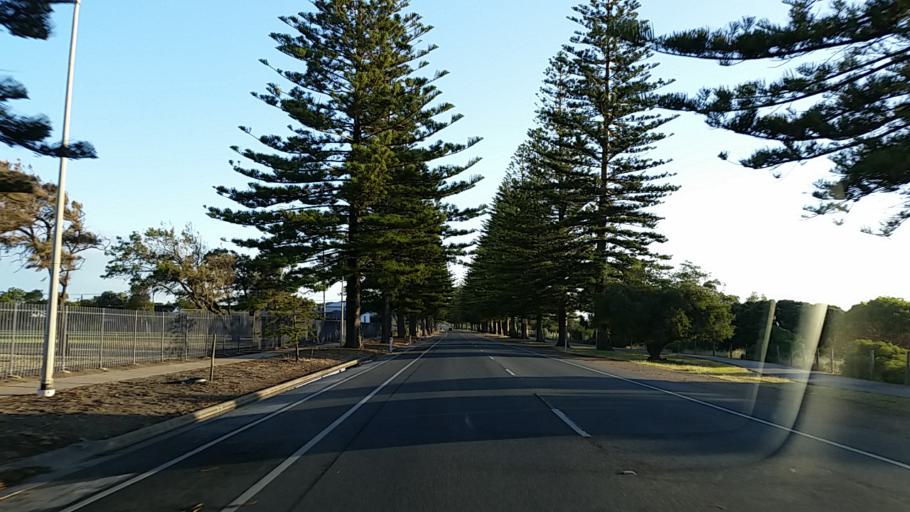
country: AU
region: South Australia
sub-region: Port Adelaide Enfield
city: Birkenhead
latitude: -34.8031
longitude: 138.4917
